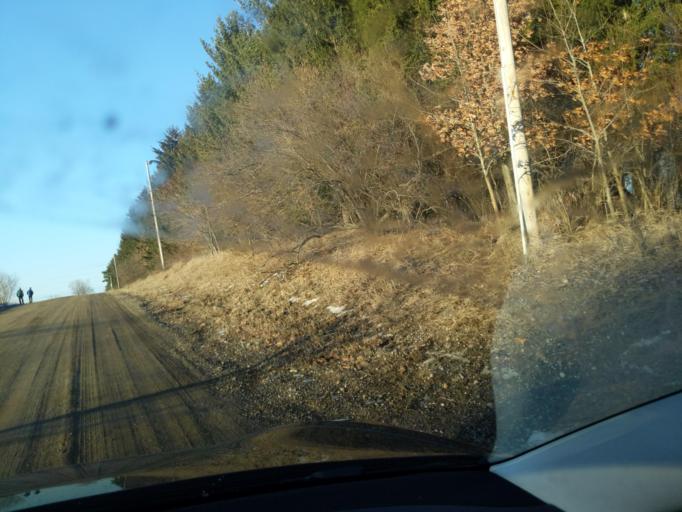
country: US
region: Michigan
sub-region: Ingham County
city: Stockbridge
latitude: 42.5417
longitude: -84.2879
